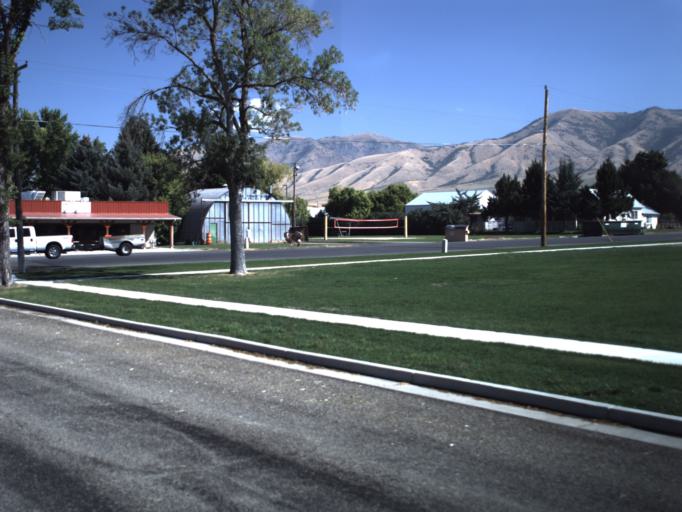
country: US
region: Utah
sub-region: Cache County
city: Hyrum
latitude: 41.5683
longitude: -111.8384
